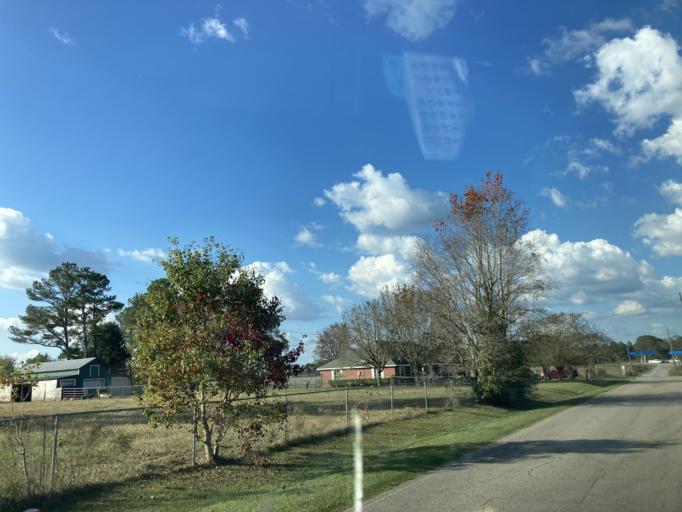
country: US
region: Mississippi
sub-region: Lamar County
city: Sumrall
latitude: 31.4329
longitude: -89.6378
